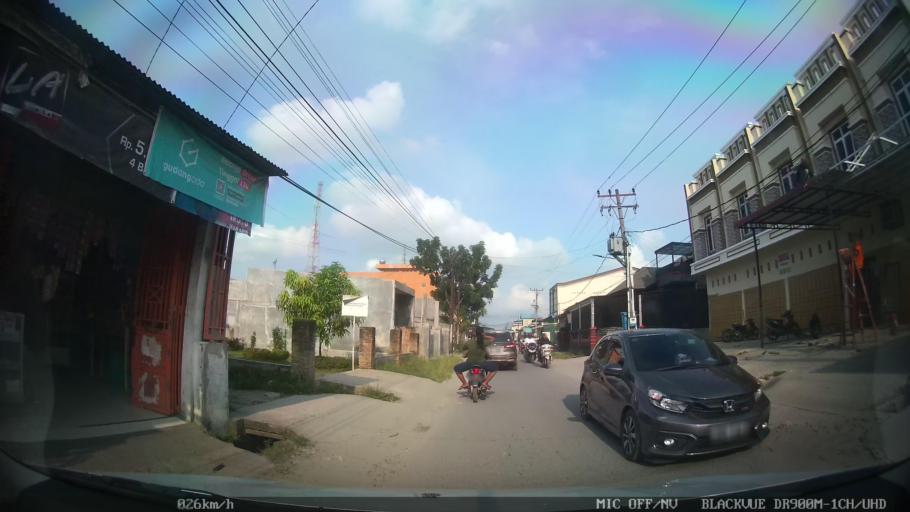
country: ID
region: North Sumatra
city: Medan
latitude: 3.5850
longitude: 98.7542
